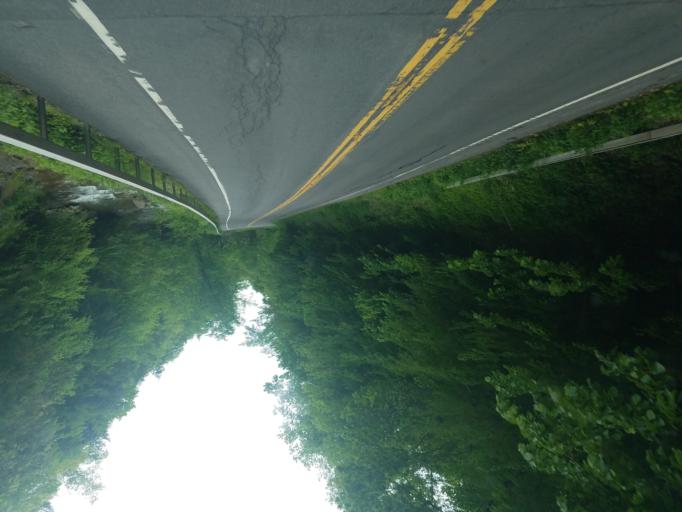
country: US
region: New York
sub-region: Herkimer County
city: Ilion
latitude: 42.9868
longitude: -75.0765
